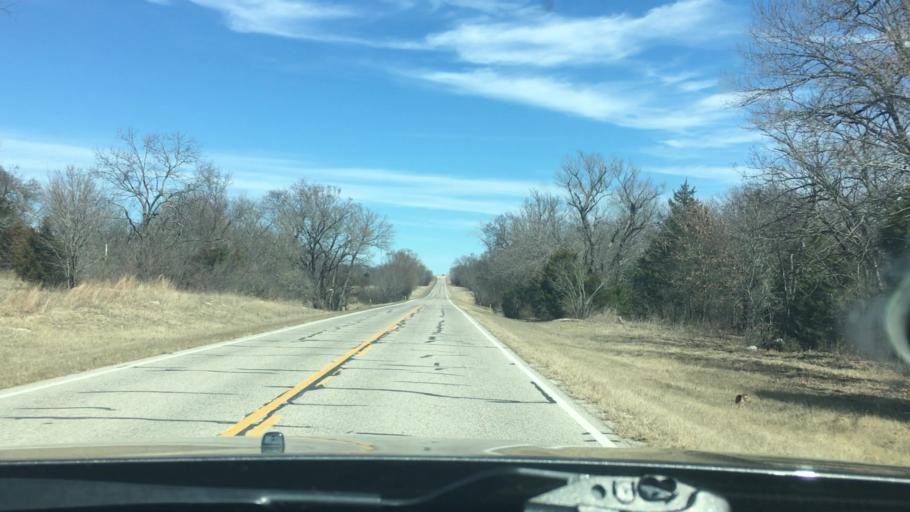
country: US
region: Oklahoma
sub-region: Carter County
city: Dickson
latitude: 34.3239
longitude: -96.9585
